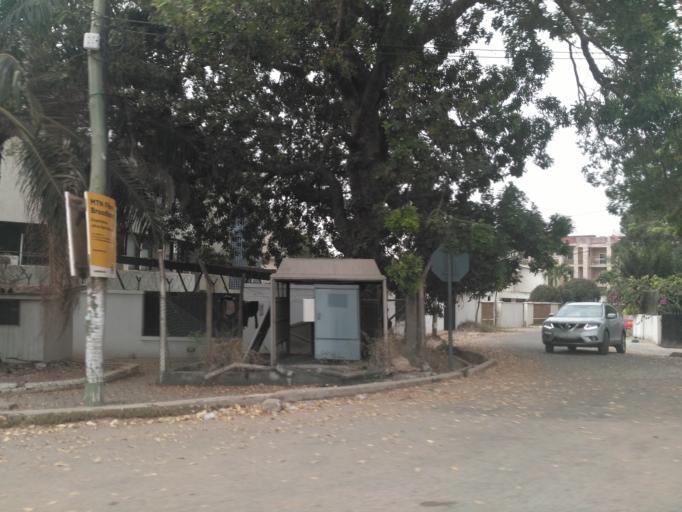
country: GH
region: Greater Accra
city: Accra
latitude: 5.5749
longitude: -0.1792
